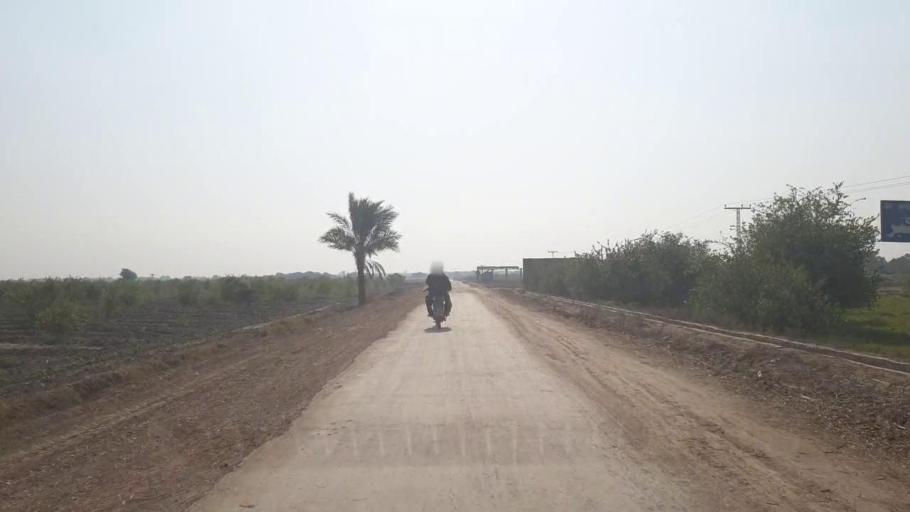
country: PK
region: Sindh
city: Tando Allahyar
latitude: 25.4634
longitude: 68.8137
